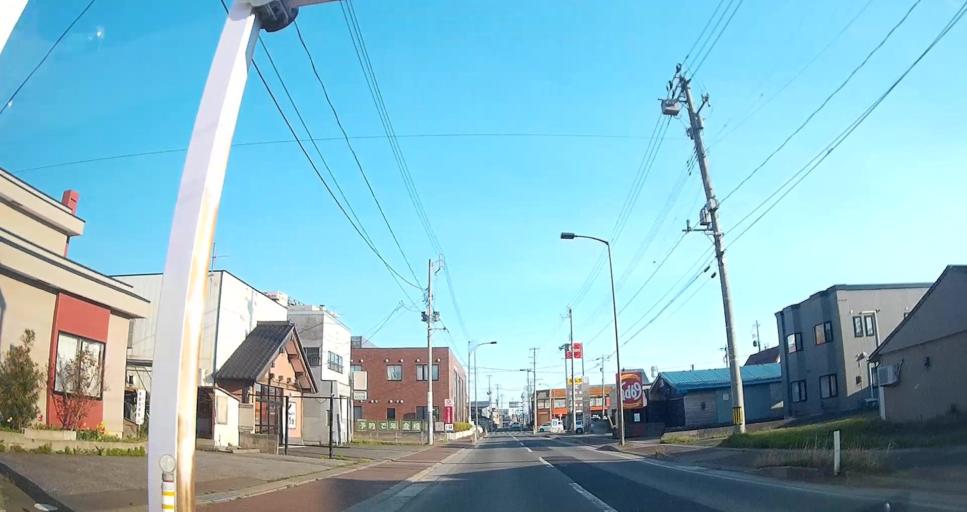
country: JP
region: Aomori
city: Mutsu
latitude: 41.2943
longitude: 141.2102
